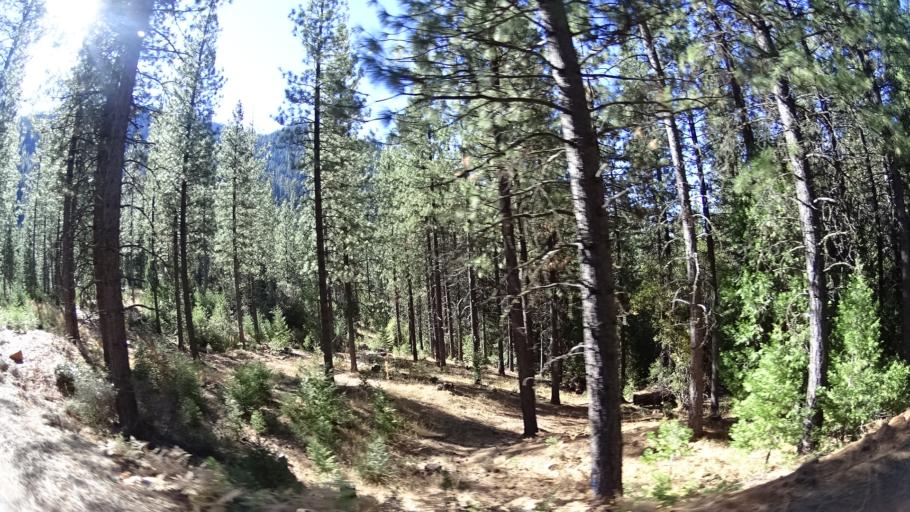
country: US
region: California
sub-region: Trinity County
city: Weaverville
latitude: 41.2267
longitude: -122.9953
